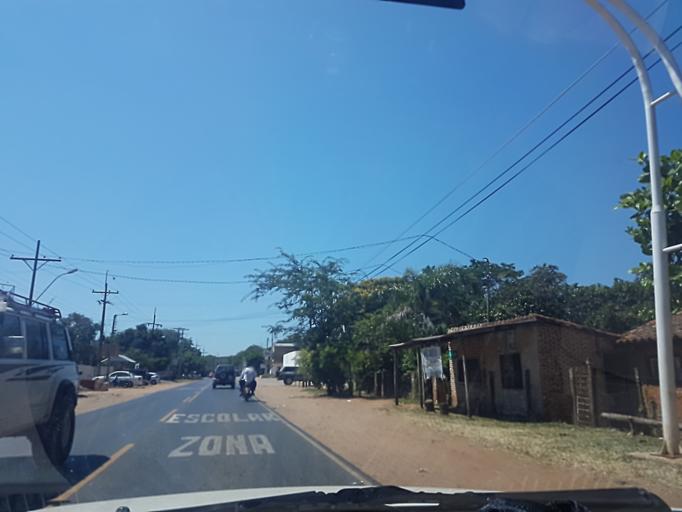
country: PY
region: Central
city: Limpio
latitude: -25.1896
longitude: -57.4642
